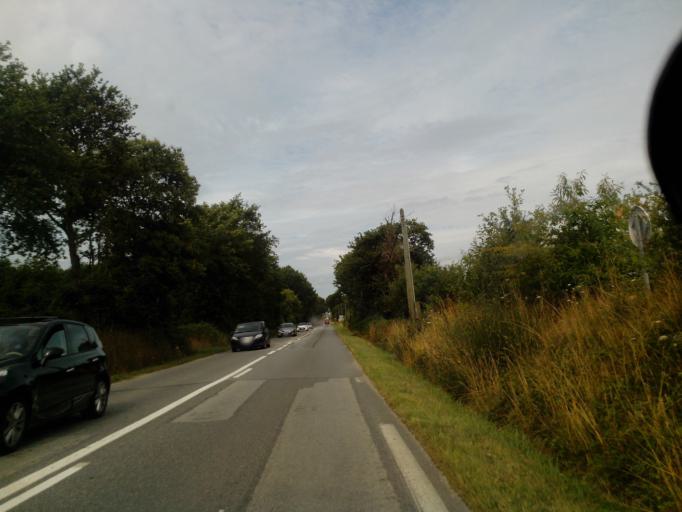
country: FR
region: Brittany
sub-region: Departement du Morbihan
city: Auray
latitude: 47.6659
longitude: -3.0260
